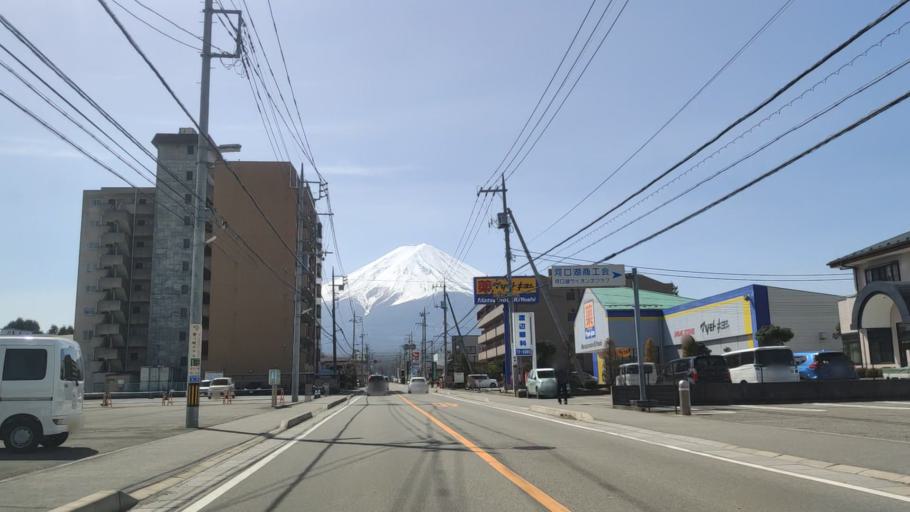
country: JP
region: Yamanashi
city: Fujikawaguchiko
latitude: 35.4955
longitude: 138.7643
